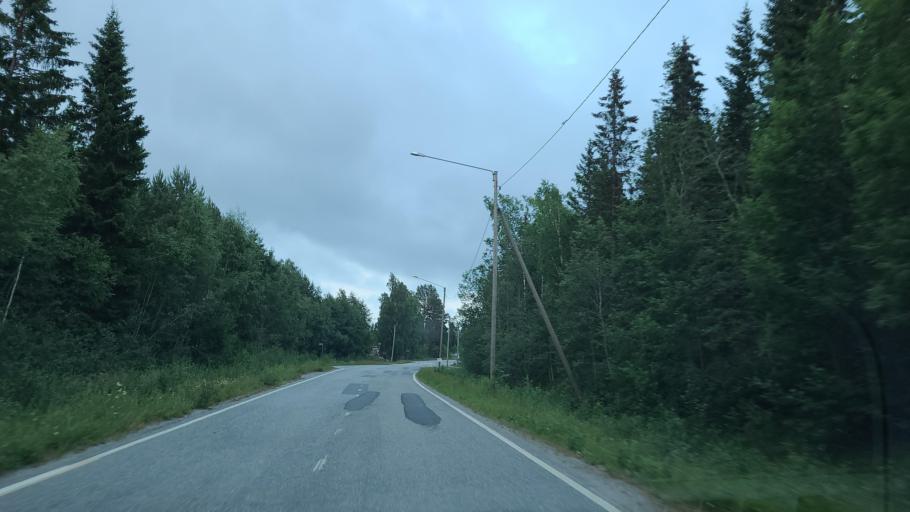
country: FI
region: Ostrobothnia
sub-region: Vaasa
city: Replot
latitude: 63.2856
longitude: 21.1195
